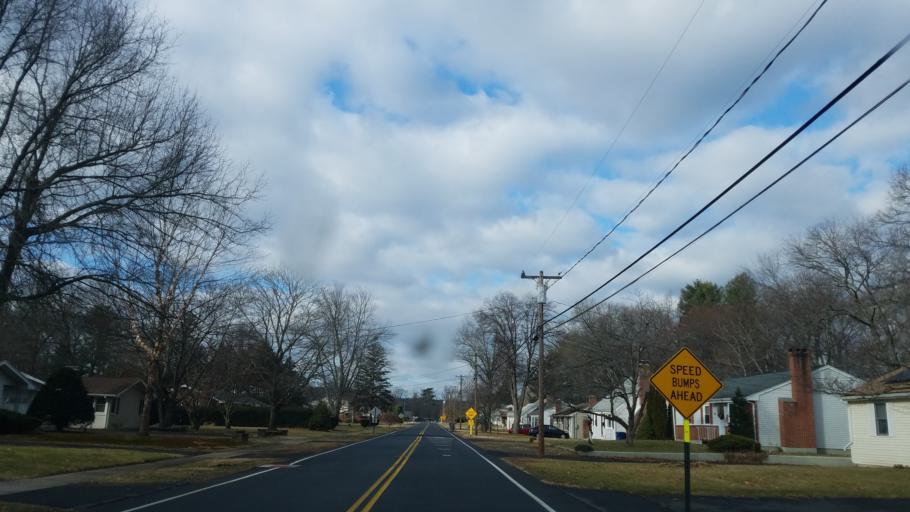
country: US
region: Connecticut
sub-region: Hartford County
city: Plainville
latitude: 41.6878
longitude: -72.8471
